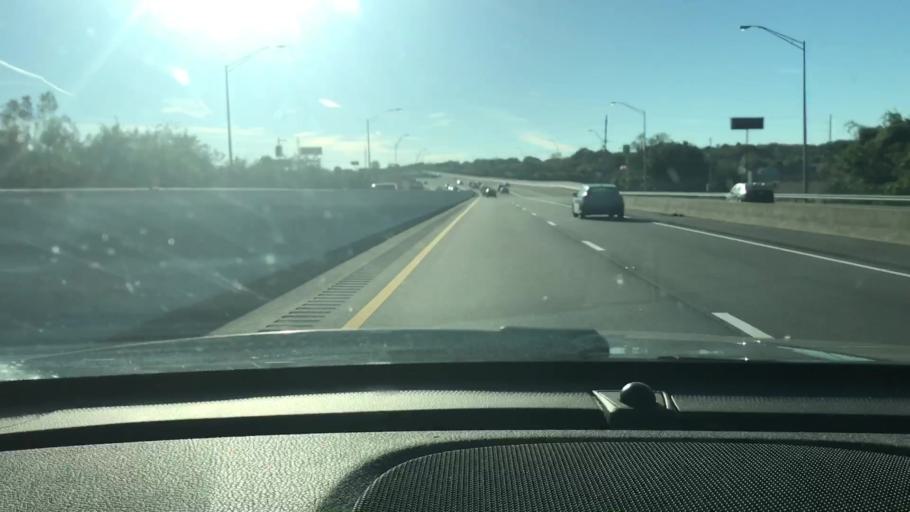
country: US
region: Tennessee
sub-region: Davidson County
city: Goodlettsville
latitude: 36.3064
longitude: -86.7004
